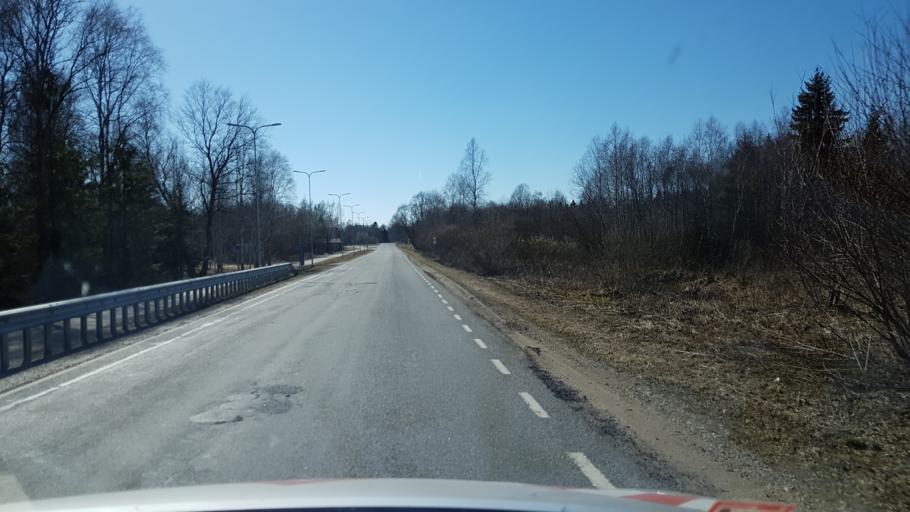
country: EE
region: Laeaene-Virumaa
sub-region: Vaeike-Maarja vald
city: Vaike-Maarja
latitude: 59.0906
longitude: 26.1793
